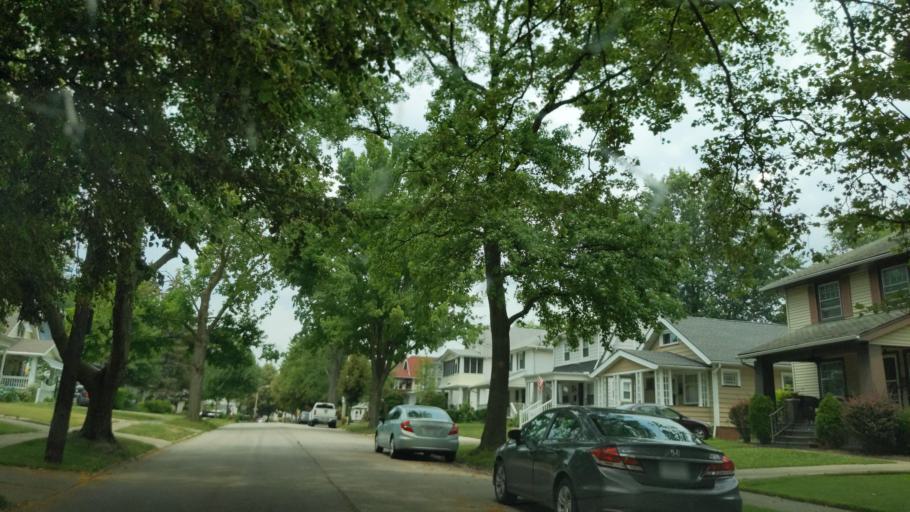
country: US
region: Ohio
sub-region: Cuyahoga County
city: Lakewood
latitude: 41.4544
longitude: -81.8001
